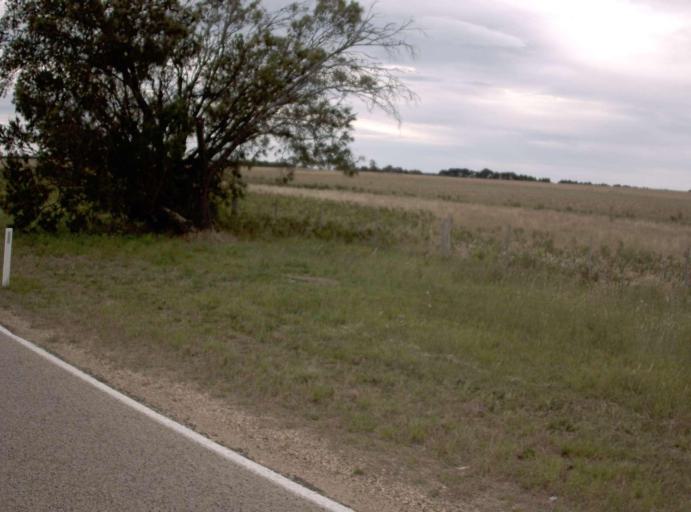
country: AU
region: Victoria
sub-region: East Gippsland
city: Bairnsdale
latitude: -37.9628
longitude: 147.4912
